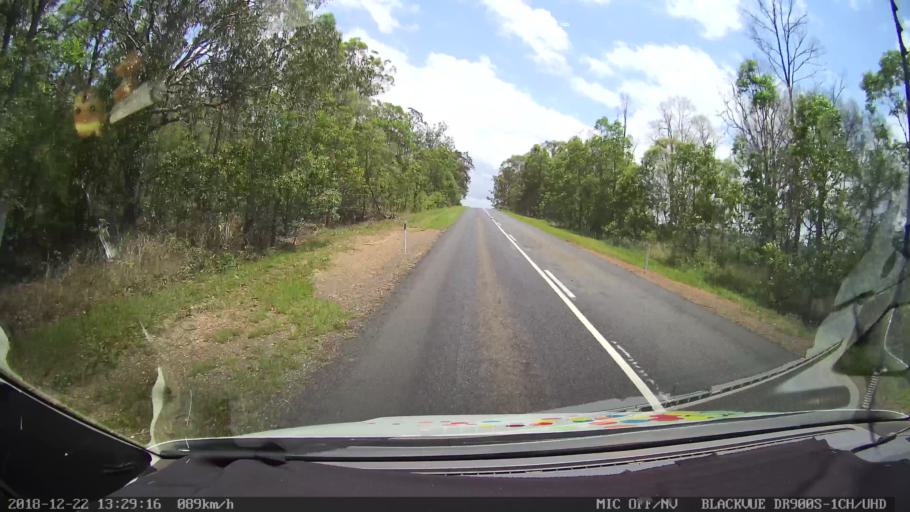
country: AU
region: New South Wales
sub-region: Clarence Valley
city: Coutts Crossing
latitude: -29.8414
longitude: 152.8794
